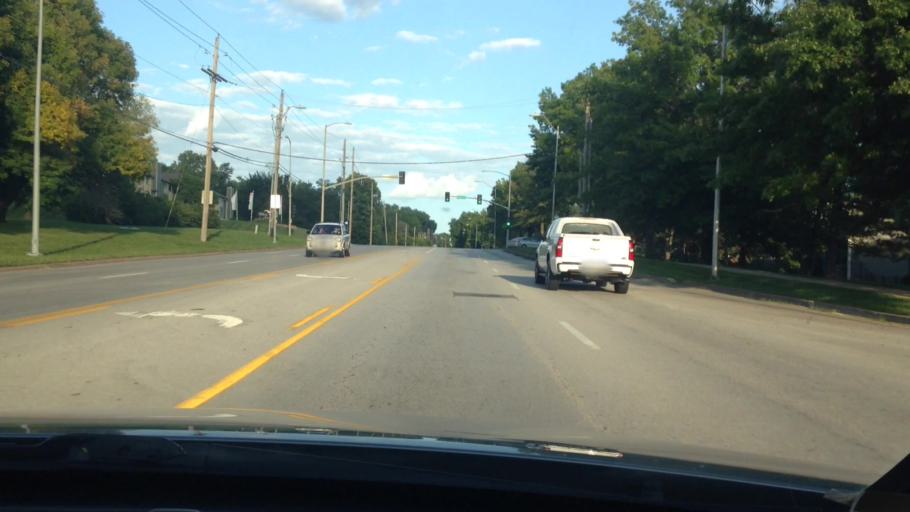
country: US
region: Missouri
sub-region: Jackson County
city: Raytown
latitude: 38.9671
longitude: -94.5120
